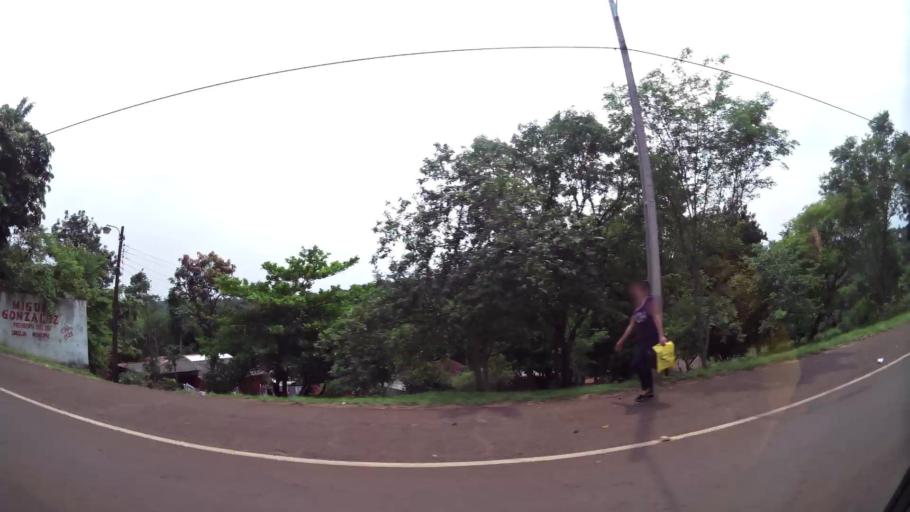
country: BR
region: Parana
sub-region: Foz Do Iguacu
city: Foz do Iguacu
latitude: -25.5507
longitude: -54.6053
